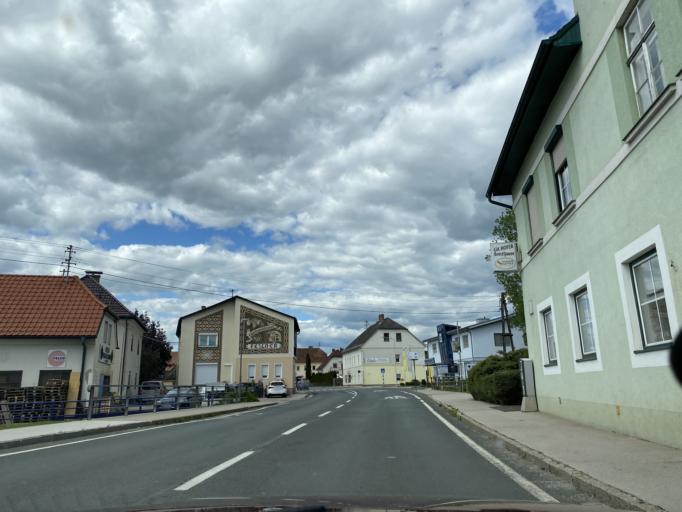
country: AT
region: Carinthia
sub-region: Politischer Bezirk Wolfsberg
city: Wolfsberg
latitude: 46.8058
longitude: 14.8496
